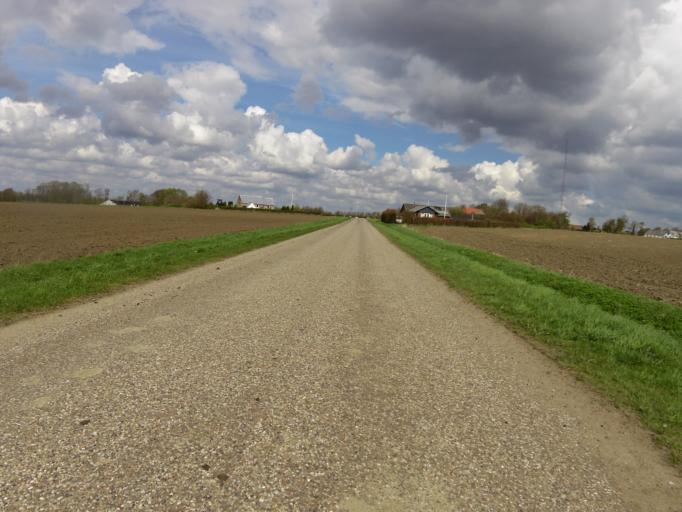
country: DK
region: South Denmark
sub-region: Tonder Kommune
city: Toftlund
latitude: 55.2088
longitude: 9.1343
